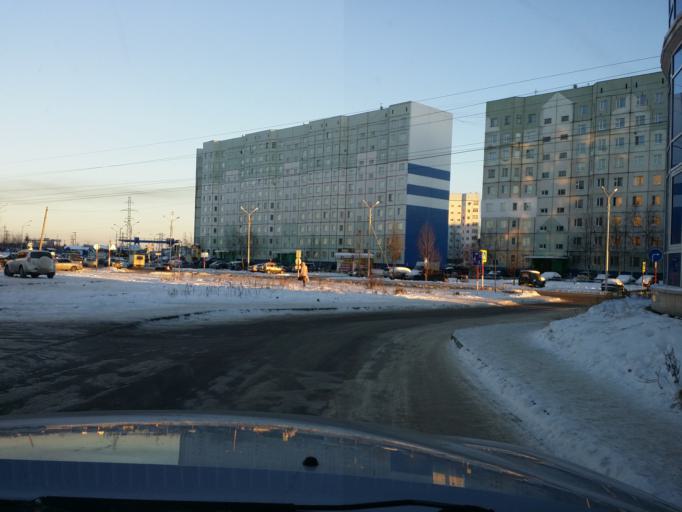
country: RU
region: Khanty-Mansiyskiy Avtonomnyy Okrug
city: Nizhnevartovsk
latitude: 60.9562
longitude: 76.5801
